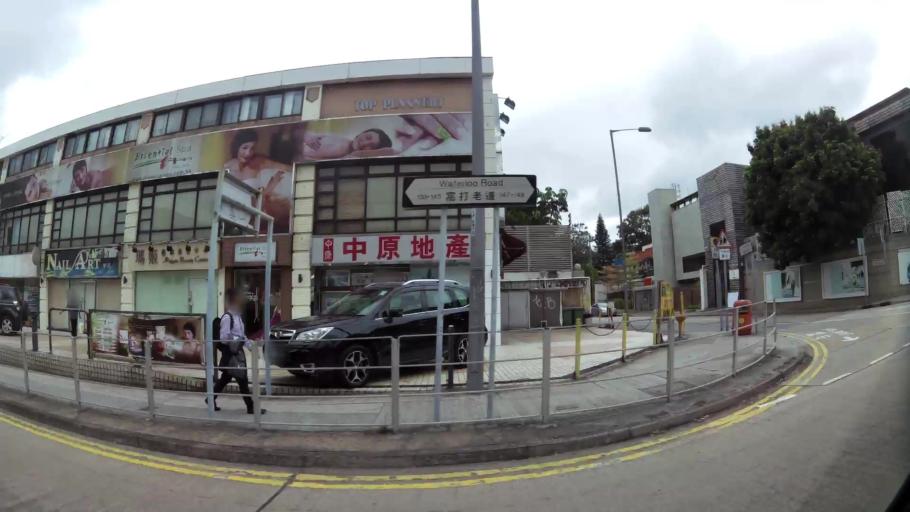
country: HK
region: Wong Tai Sin
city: Wong Tai Sin
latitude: 22.3378
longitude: 114.1789
